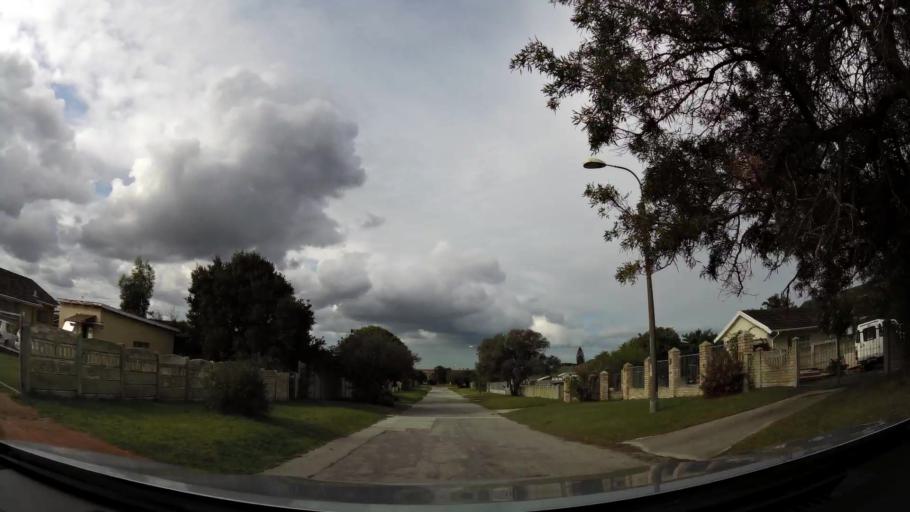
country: ZA
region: Eastern Cape
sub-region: Nelson Mandela Bay Metropolitan Municipality
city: Port Elizabeth
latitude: -33.9367
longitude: 25.4963
